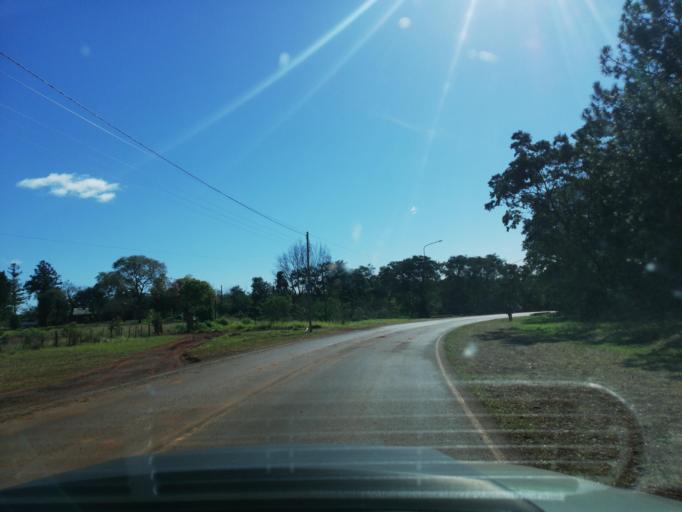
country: AR
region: Misiones
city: Aristobulo del Valle
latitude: -27.0892
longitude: -54.9158
